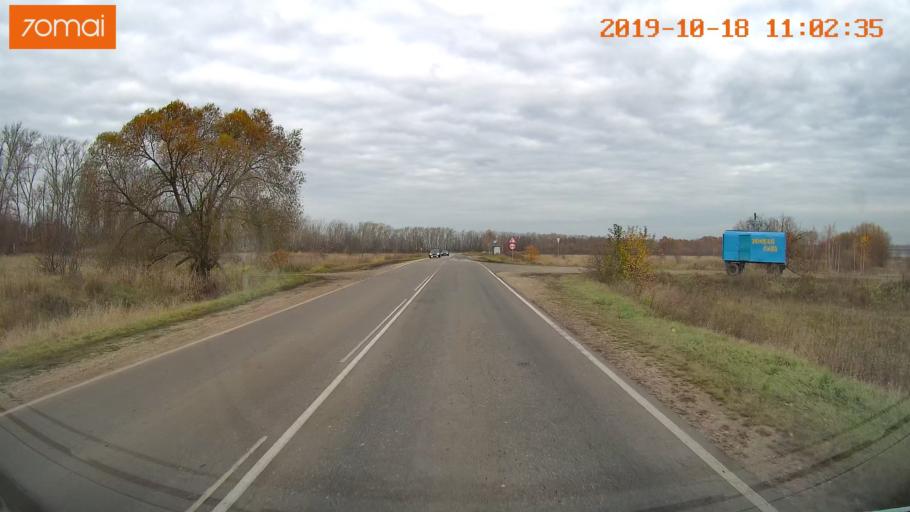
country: RU
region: Tula
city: Yepifan'
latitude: 53.8677
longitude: 38.5440
